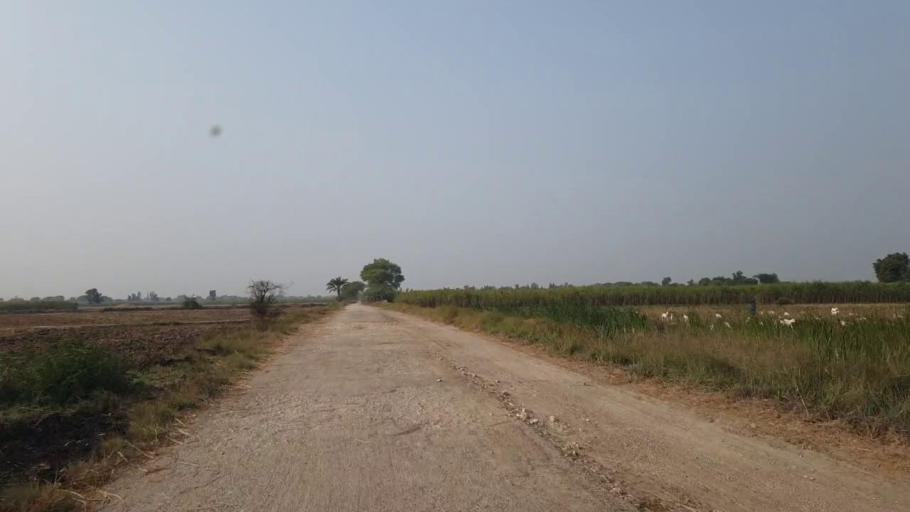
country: PK
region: Sindh
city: Matli
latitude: 25.0758
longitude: 68.5918
